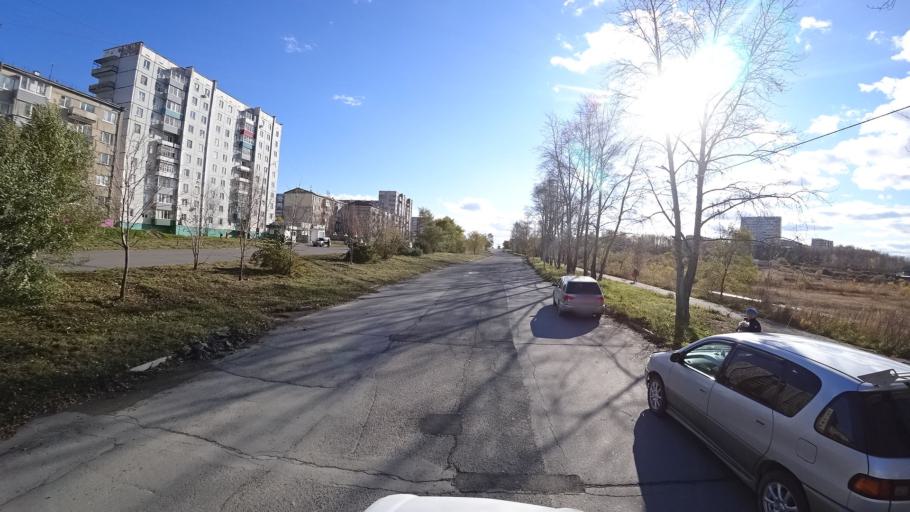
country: RU
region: Khabarovsk Krai
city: Amursk
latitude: 50.2464
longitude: 136.9159
